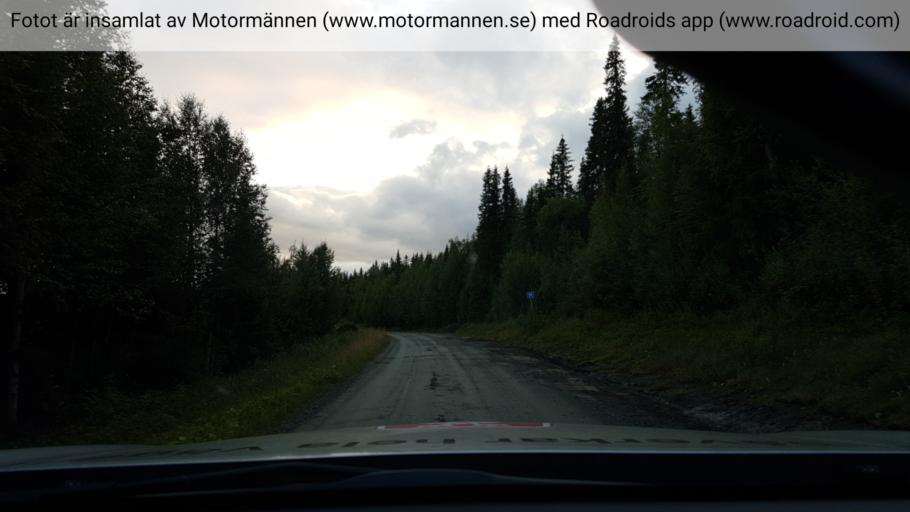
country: SE
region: Vaesterbotten
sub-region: Vilhelmina Kommun
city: Sjoberg
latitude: 65.4986
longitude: 15.5395
